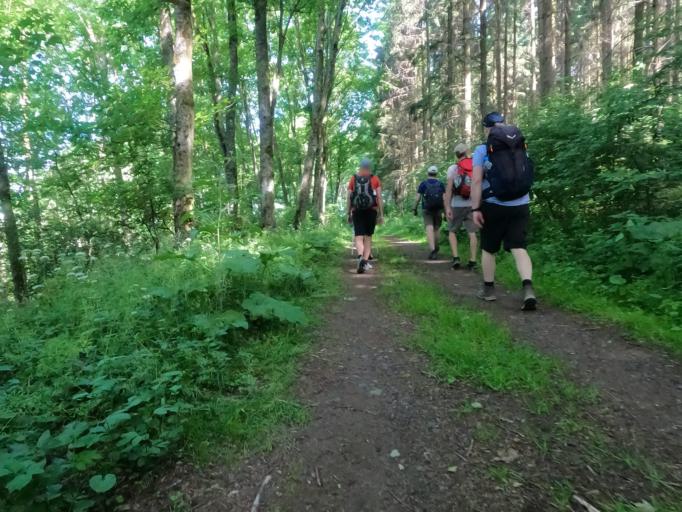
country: DE
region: Rheinland-Pfalz
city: Bolsberg
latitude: 50.6596
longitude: 7.9117
